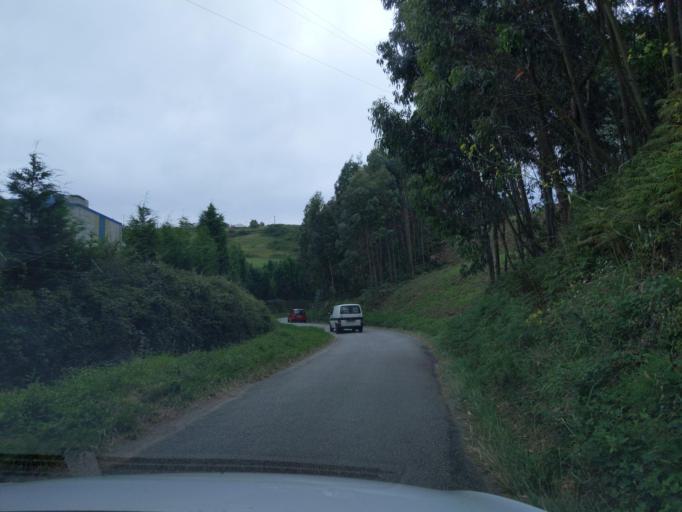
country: ES
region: Asturias
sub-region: Province of Asturias
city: Aviles
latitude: 43.5994
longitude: -5.9133
